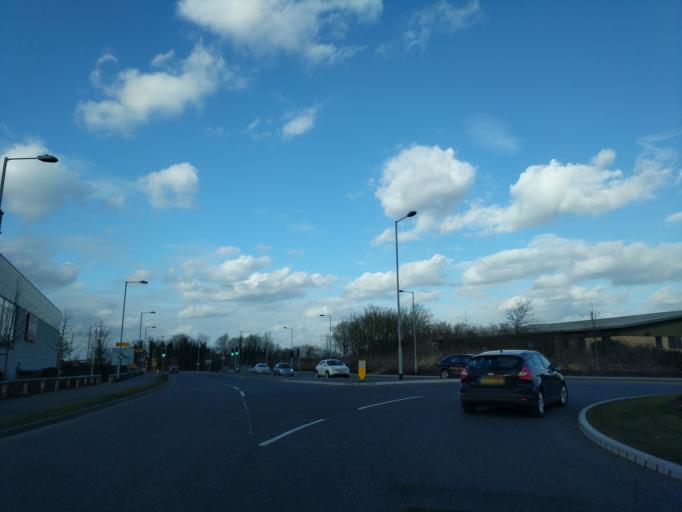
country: GB
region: England
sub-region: Central Bedfordshire
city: Biggleswade
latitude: 52.0747
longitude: -0.2437
